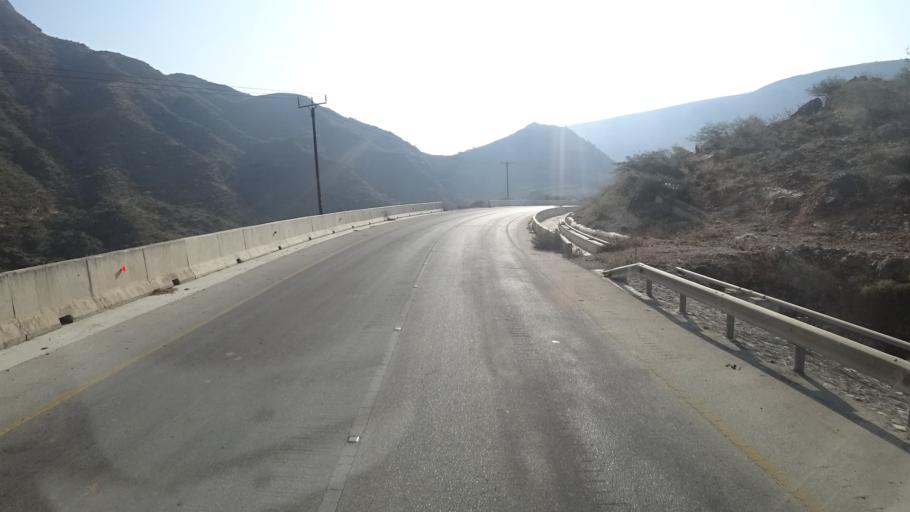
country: YE
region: Al Mahrah
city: Hawf
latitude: 16.7468
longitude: 53.2283
